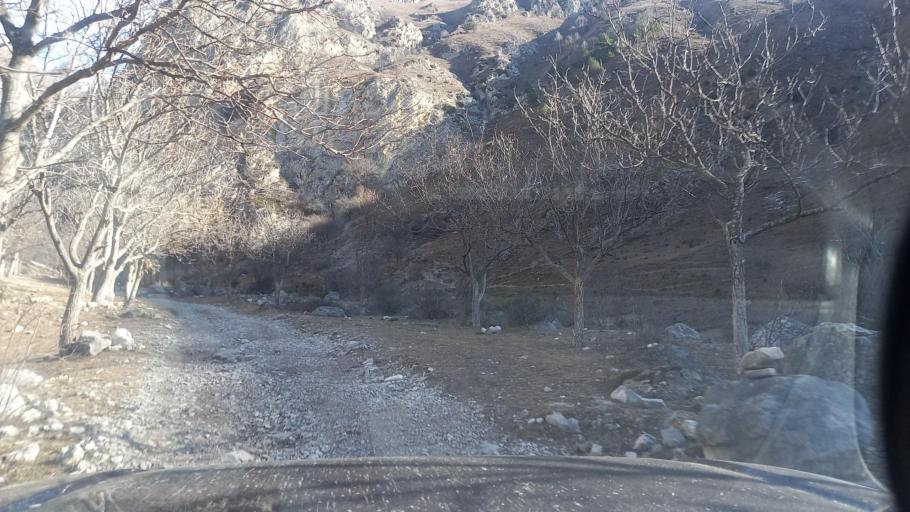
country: RU
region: Ingushetiya
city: Dzhayrakh
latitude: 42.8451
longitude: 44.6640
